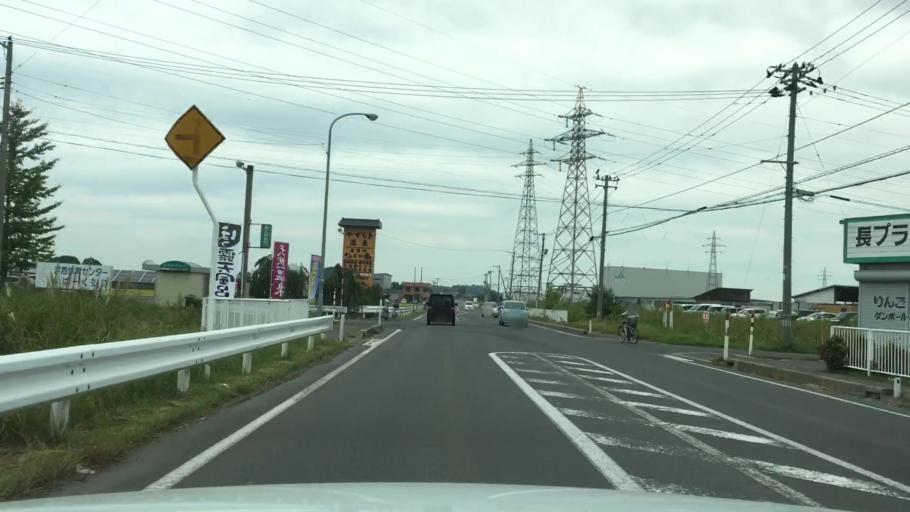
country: JP
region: Aomori
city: Hirosaki
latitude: 40.6330
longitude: 140.4509
